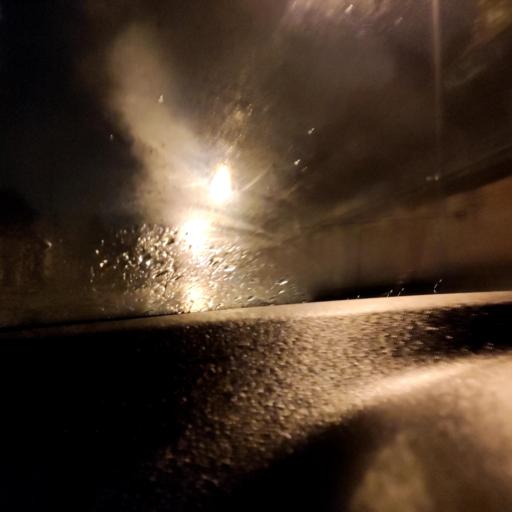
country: RU
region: Samara
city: Samara
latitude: 53.2783
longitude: 50.1919
